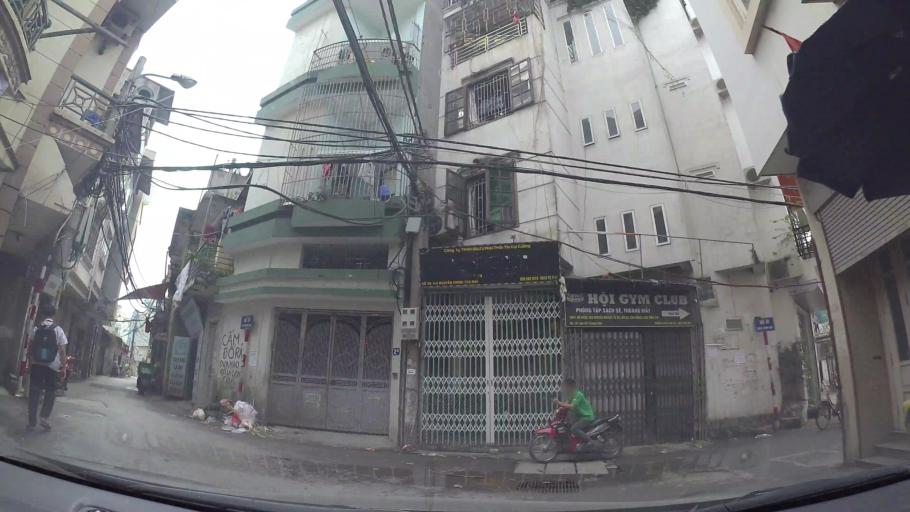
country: VN
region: Ha Noi
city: Van Dien
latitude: 20.9782
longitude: 105.8483
